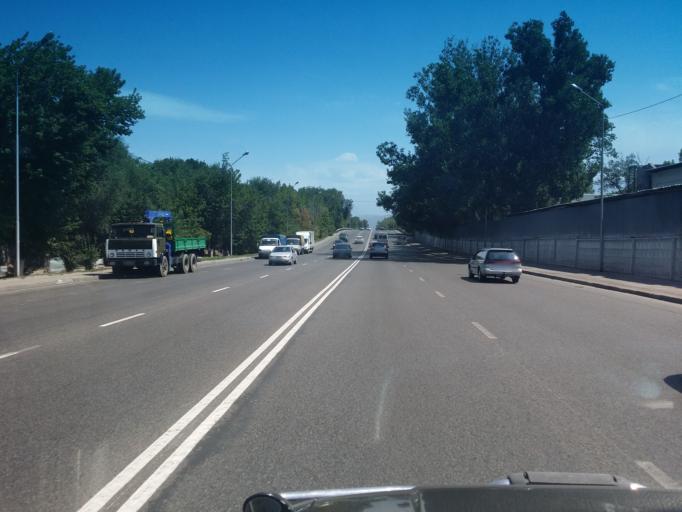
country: KZ
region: Almaty Oblysy
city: Pervomayskiy
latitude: 43.3438
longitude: 76.9742
